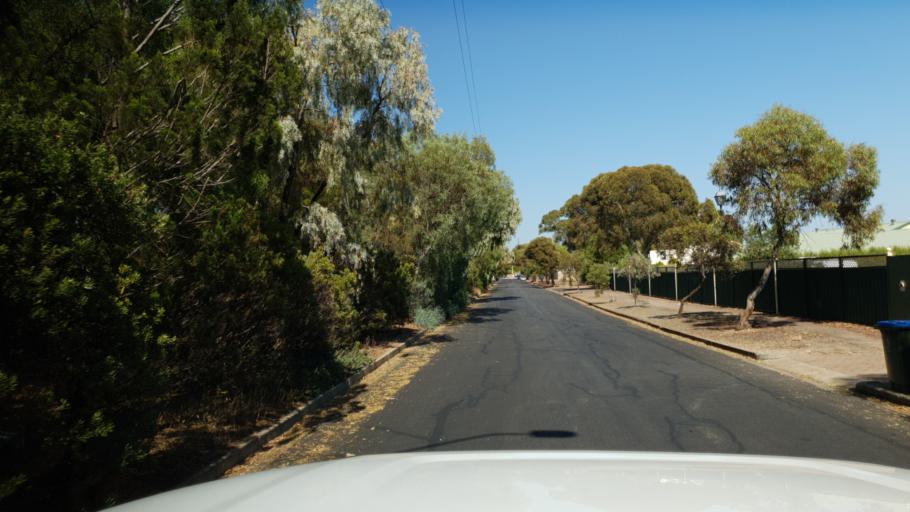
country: AU
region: South Australia
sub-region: Marion
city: Clovelly Park
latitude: -34.9961
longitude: 138.5856
